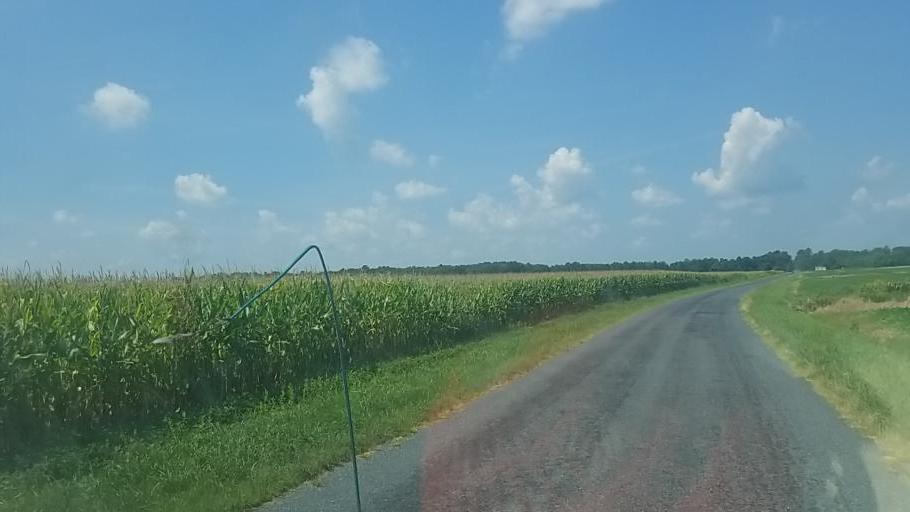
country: US
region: Maryland
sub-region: Worcester County
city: Berlin
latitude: 38.2978
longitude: -75.2753
